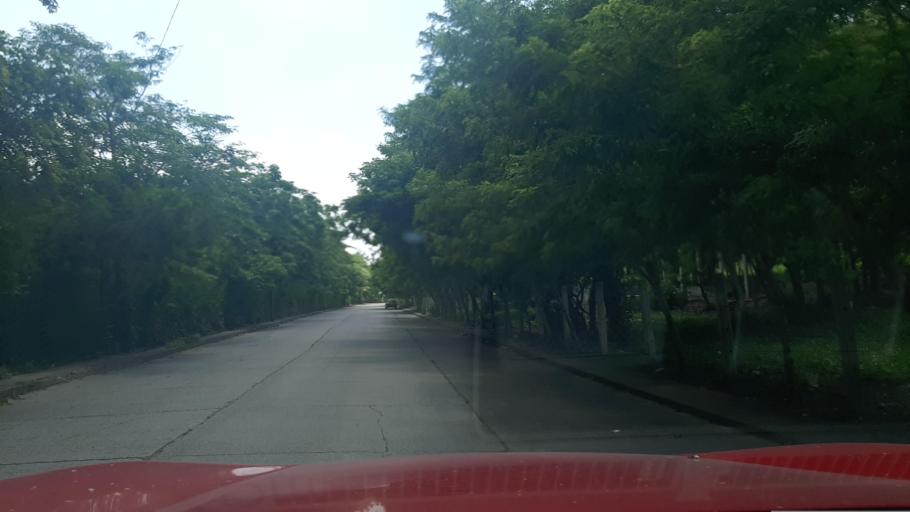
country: MX
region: Veracruz
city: Coatzintla
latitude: 20.4975
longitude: -97.4351
